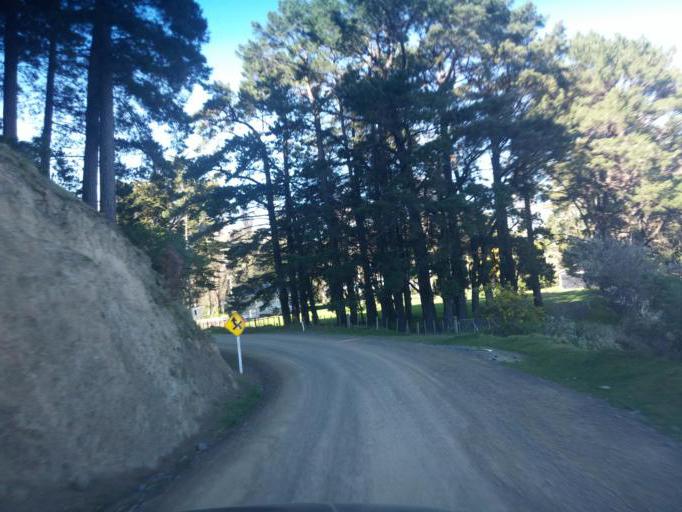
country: NZ
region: Wellington
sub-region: South Wairarapa District
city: Waipawa
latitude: -41.4418
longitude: 175.5213
